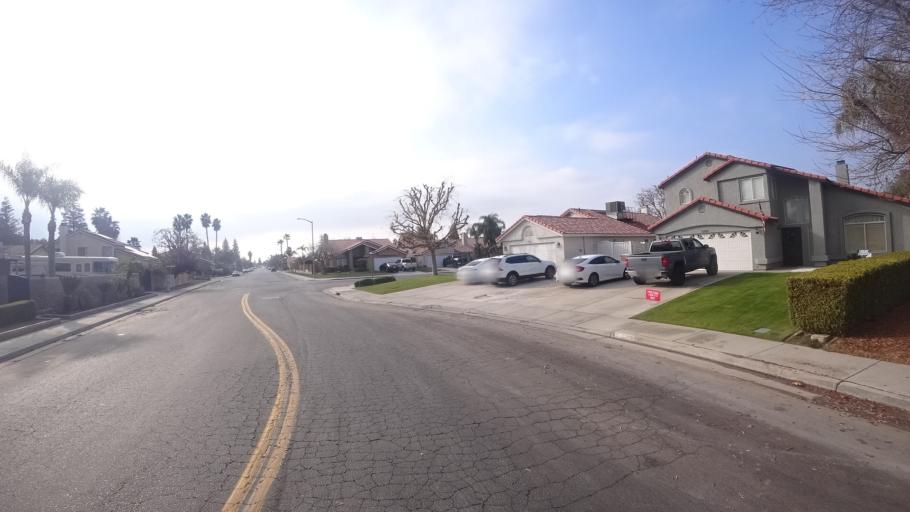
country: US
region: California
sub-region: Kern County
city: Greenfield
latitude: 35.3064
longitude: -119.0726
